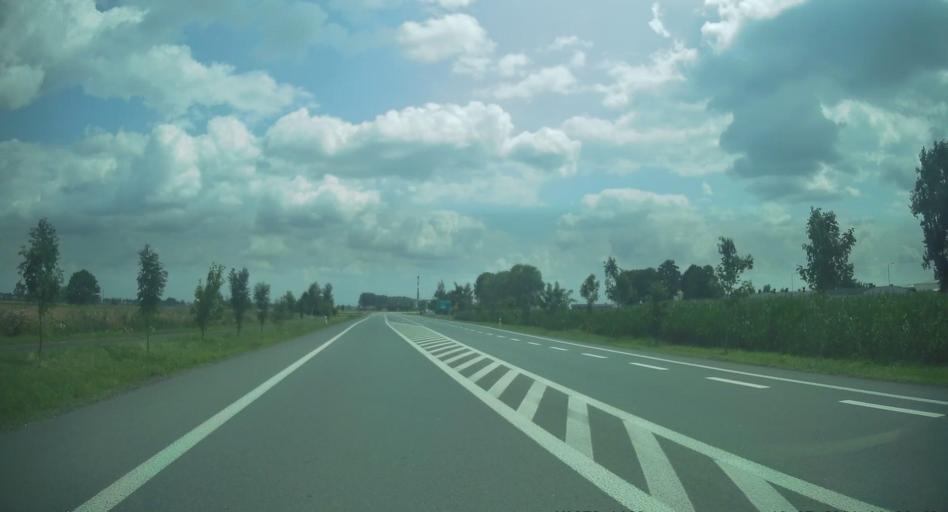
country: PL
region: Opole Voivodeship
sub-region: Powiat prudnicki
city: Prudnik
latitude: 50.3350
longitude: 17.5858
